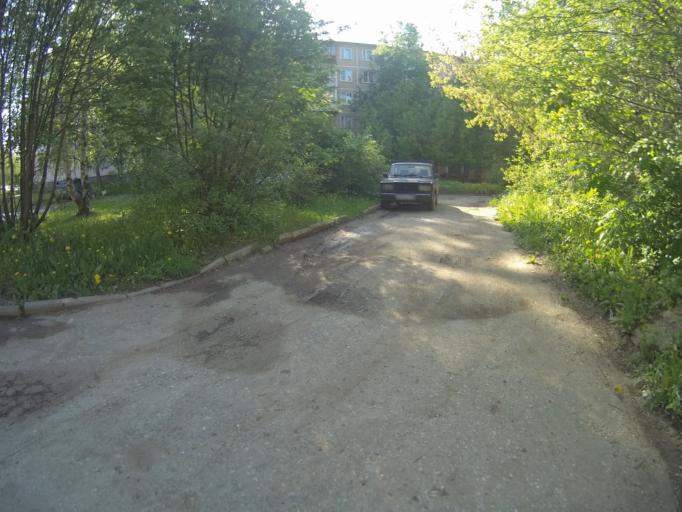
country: RU
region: Vladimir
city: Bogolyubovo
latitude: 56.1736
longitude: 40.4881
